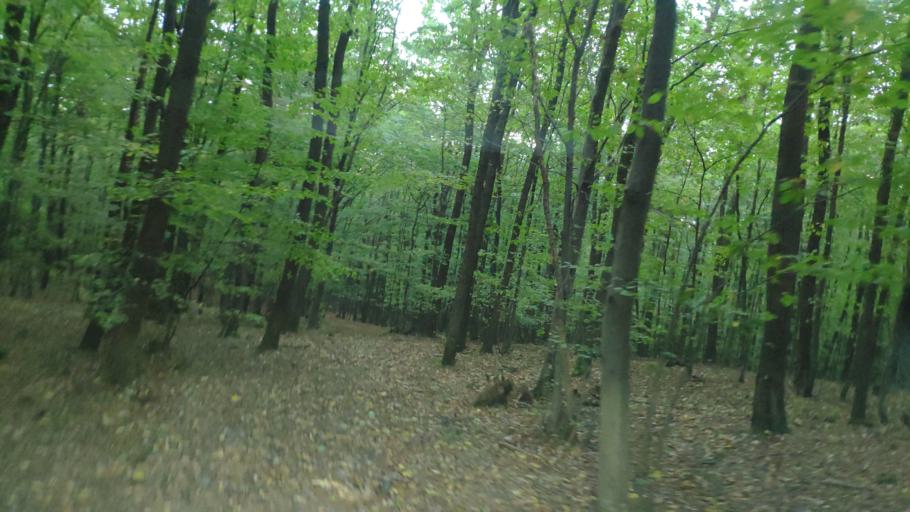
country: SK
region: Kosicky
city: Kosice
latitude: 48.6973
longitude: 21.1972
